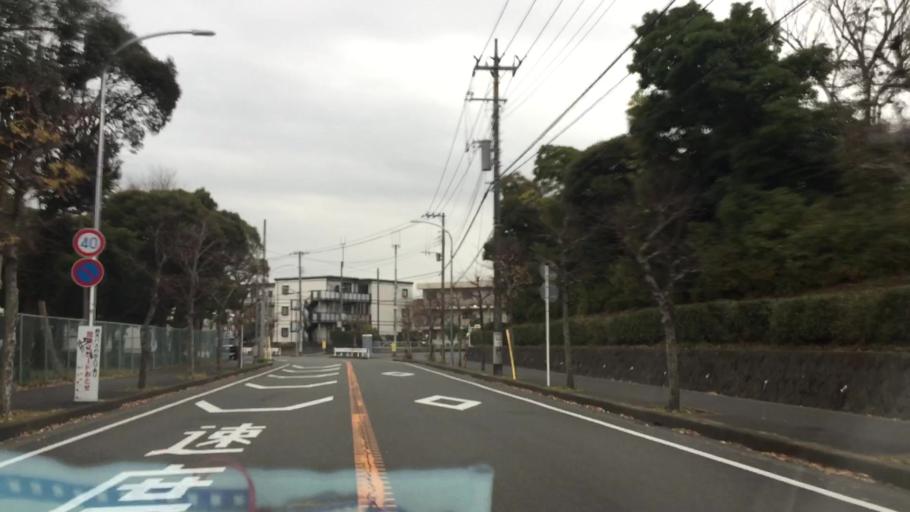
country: JP
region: Kanagawa
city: Zushi
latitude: 35.3385
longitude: 139.5980
